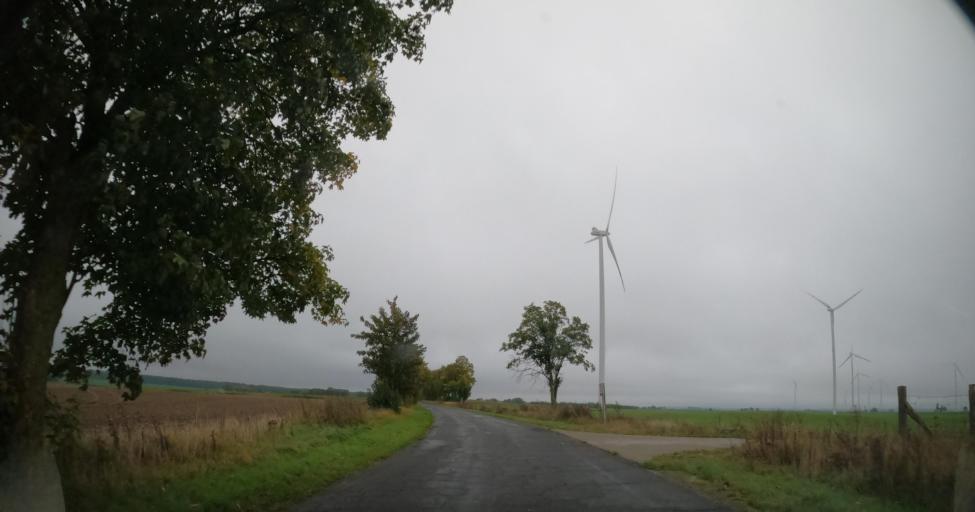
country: PL
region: West Pomeranian Voivodeship
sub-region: Powiat pyrzycki
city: Kozielice
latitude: 53.0795
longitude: 14.7794
